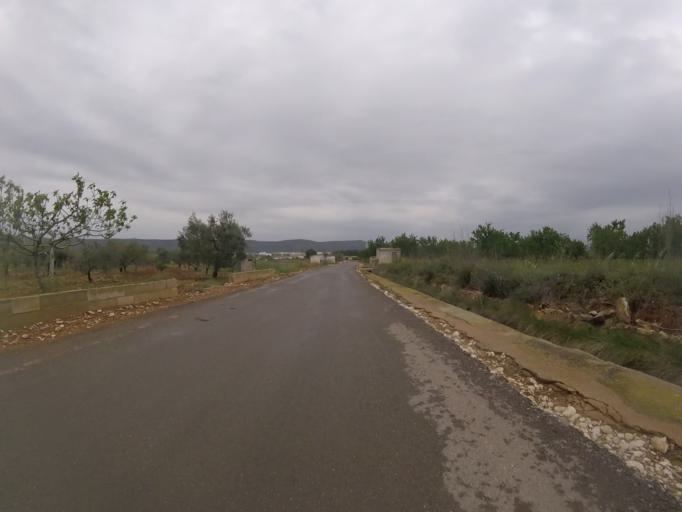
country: ES
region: Valencia
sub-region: Provincia de Castello
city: Alcala de Xivert
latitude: 40.2928
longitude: 0.2296
